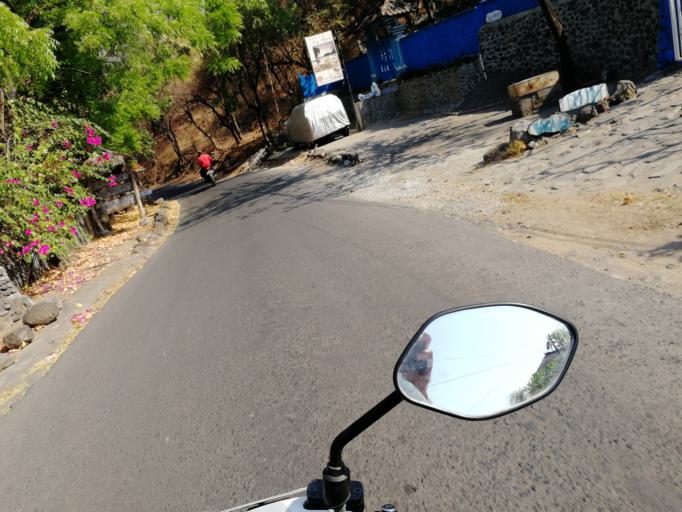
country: ID
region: Bali
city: Biaslantang Kaler
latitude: -8.3426
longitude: 115.6678
